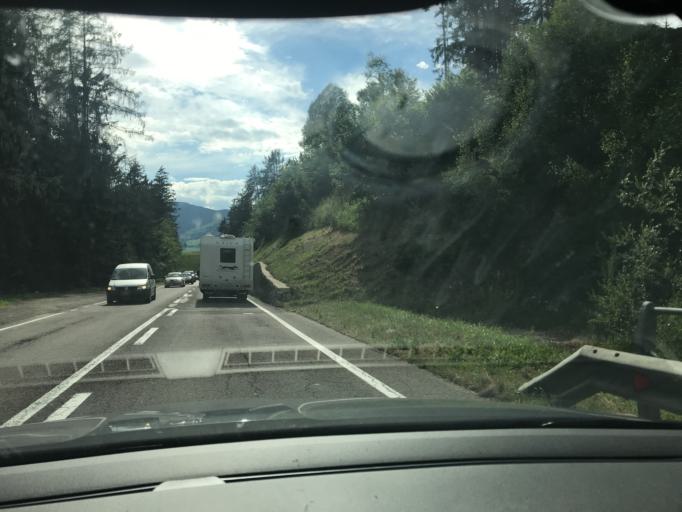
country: IT
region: Trentino-Alto Adige
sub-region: Bolzano
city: Monguelfo
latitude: 46.7631
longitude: 12.0803
